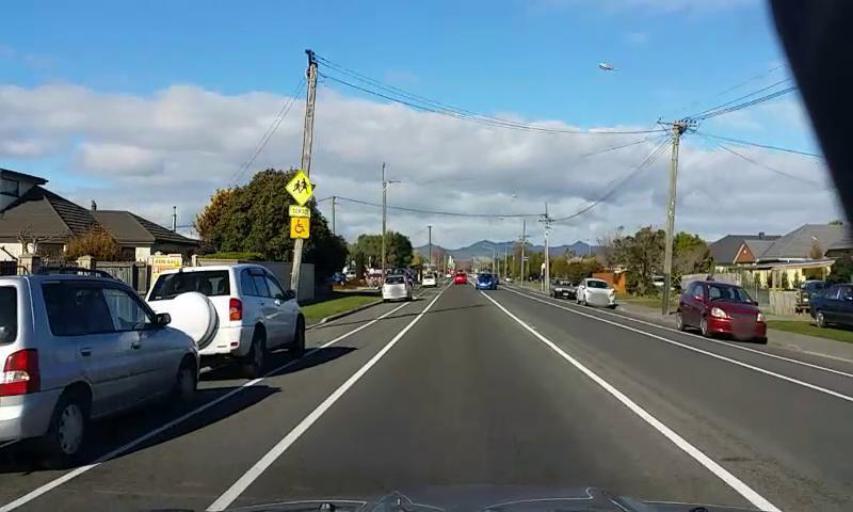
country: NZ
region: Canterbury
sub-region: Christchurch City
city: Christchurch
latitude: -43.5002
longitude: 172.6621
